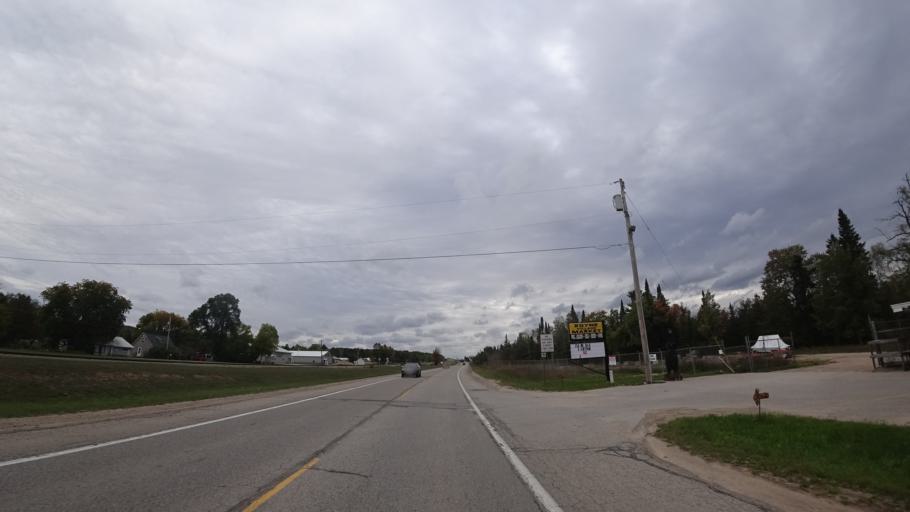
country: US
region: Michigan
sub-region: Charlevoix County
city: Boyne City
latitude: 45.1742
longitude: -84.9142
